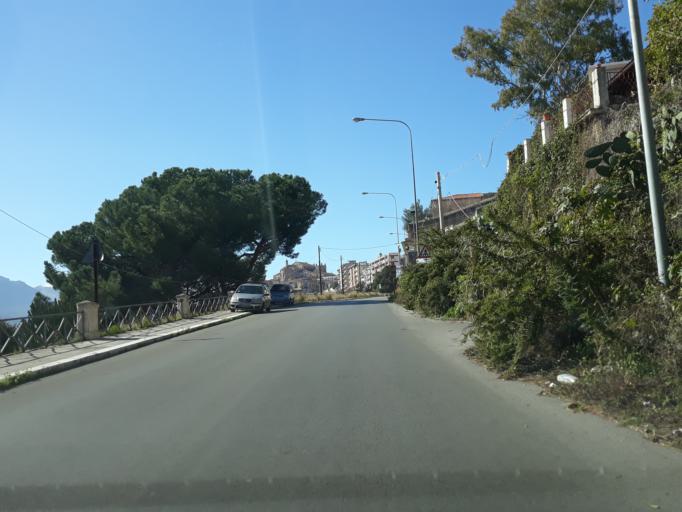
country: IT
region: Sicily
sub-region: Palermo
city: Monreale
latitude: 38.0873
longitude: 13.2975
